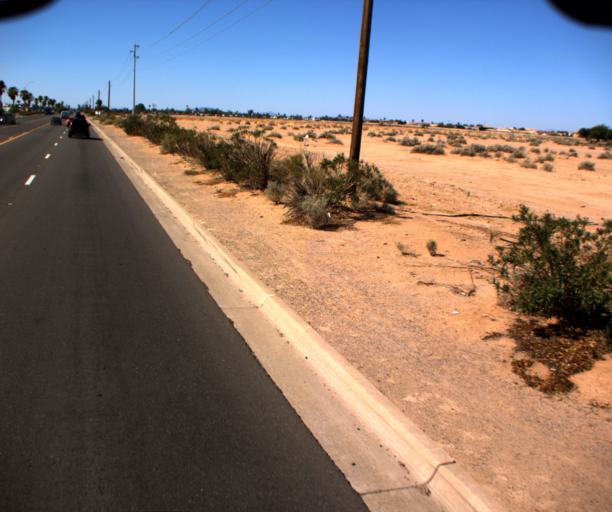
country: US
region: Arizona
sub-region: Pinal County
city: Casa Grande
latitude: 32.9069
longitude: -111.7574
